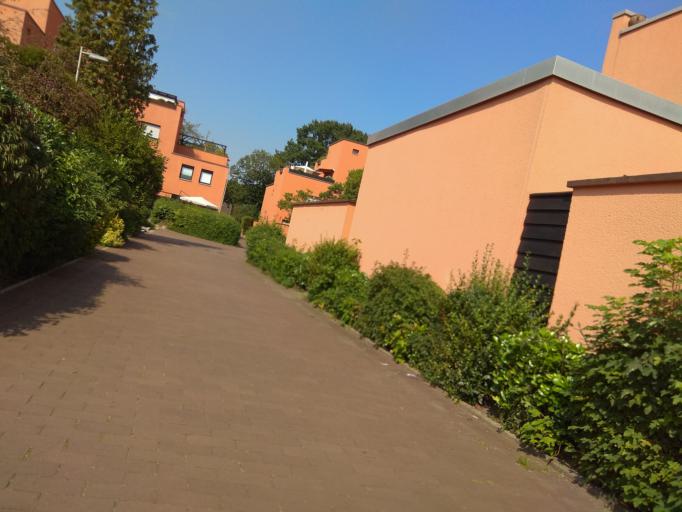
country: DE
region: North Rhine-Westphalia
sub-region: Regierungsbezirk Munster
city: Klein Reken
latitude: 51.7284
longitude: 7.0361
